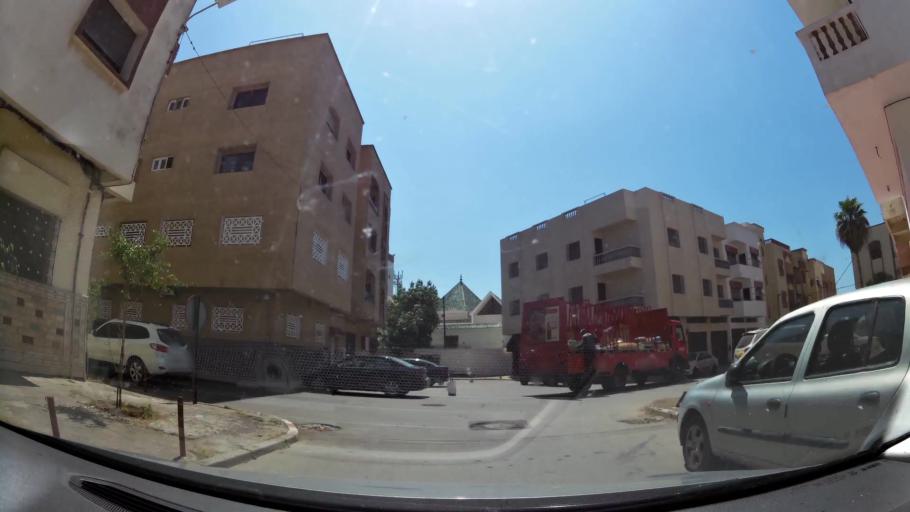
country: MA
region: Rabat-Sale-Zemmour-Zaer
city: Sale
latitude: 34.0469
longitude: -6.7872
